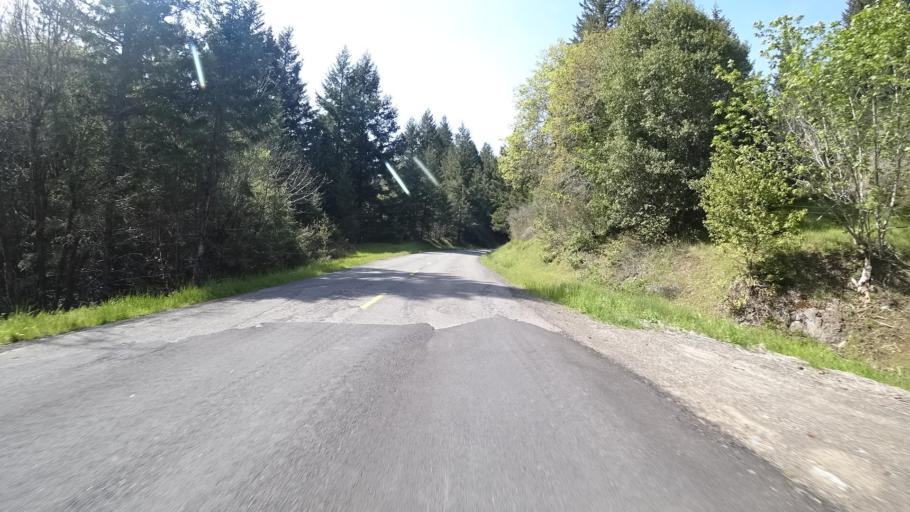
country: US
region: California
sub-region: Humboldt County
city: Rio Dell
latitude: 40.4446
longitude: -123.7944
